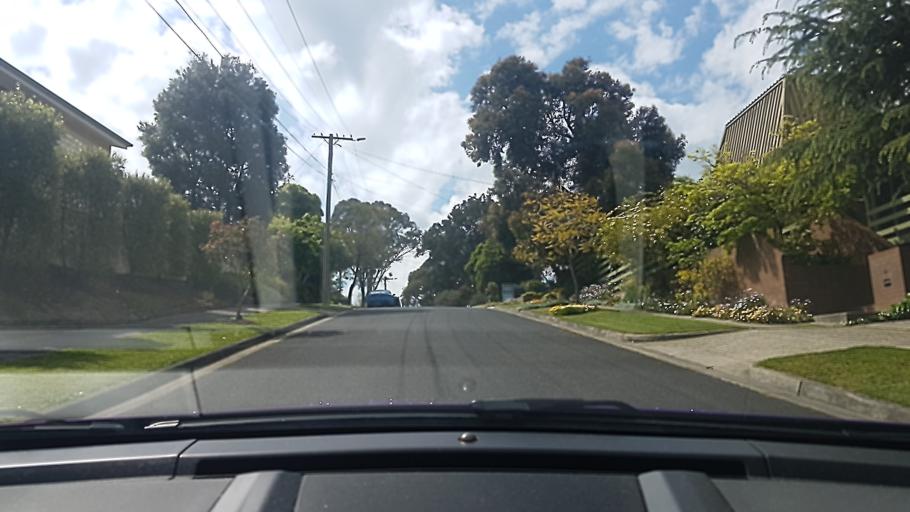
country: AU
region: Victoria
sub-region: Banyule
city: Darch
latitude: -37.7572
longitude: 145.1056
